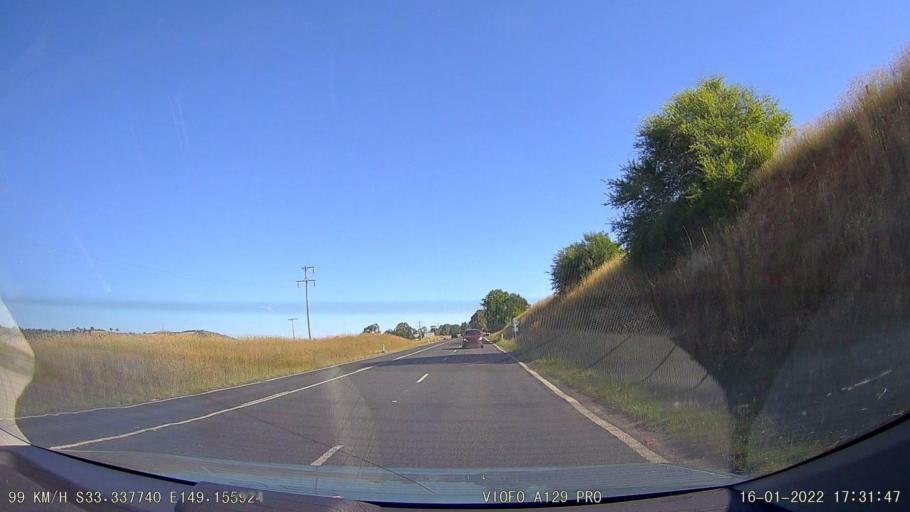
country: AU
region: New South Wales
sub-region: Orange Municipality
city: Orange
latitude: -33.3384
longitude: 149.1557
